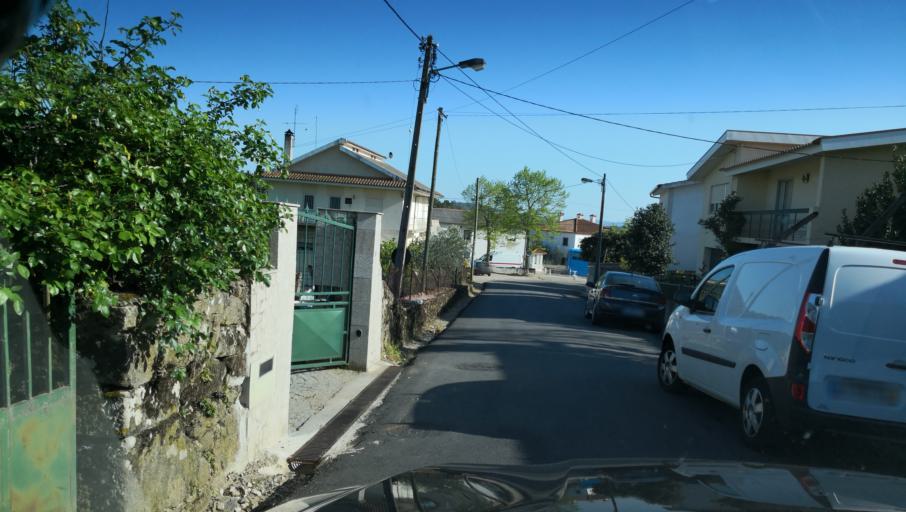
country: PT
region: Vila Real
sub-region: Vila Real
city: Vila Real
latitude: 41.2816
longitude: -7.6840
